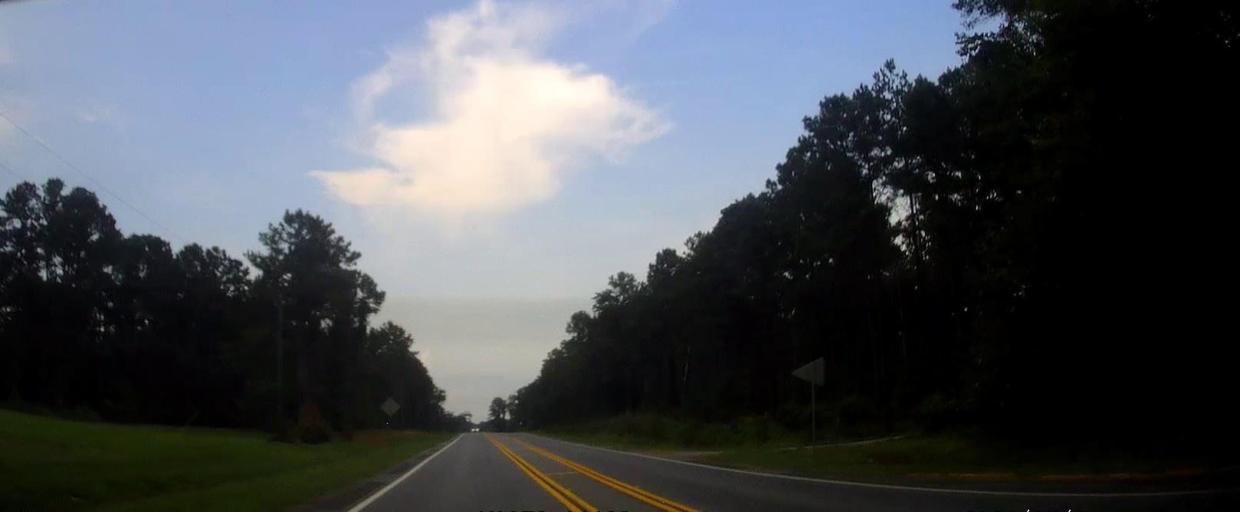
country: US
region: Georgia
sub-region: Laurens County
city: East Dublin
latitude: 32.6040
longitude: -82.8218
